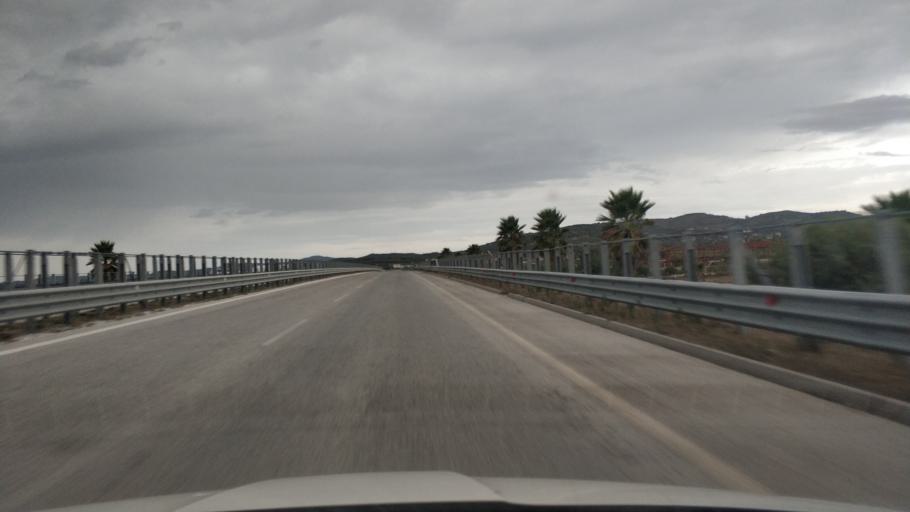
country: AL
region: Vlore
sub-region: Rrethi i Vlores
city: Novosele
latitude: 40.5559
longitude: 19.4621
